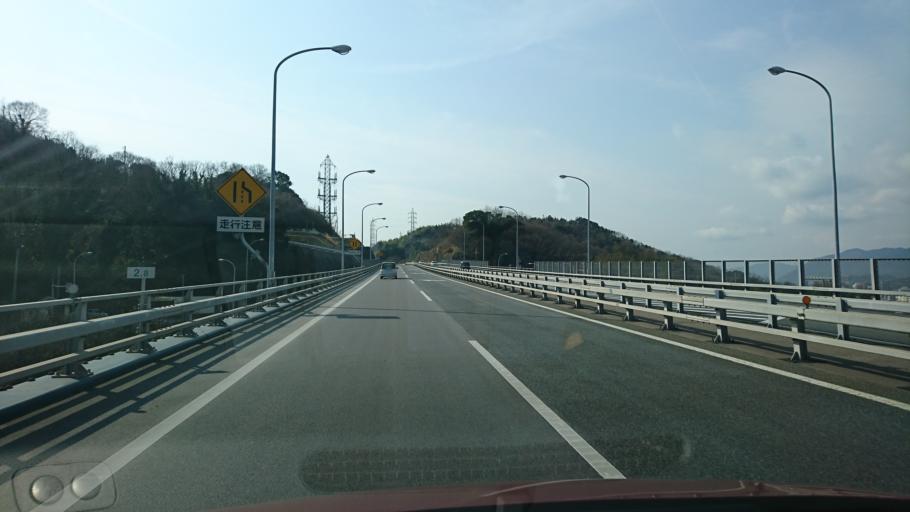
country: JP
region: Hiroshima
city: Onomichi
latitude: 34.4084
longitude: 133.2151
